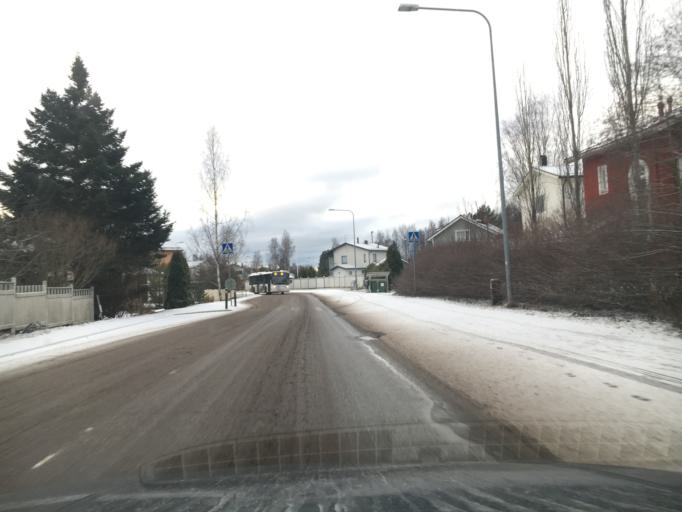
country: FI
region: Uusimaa
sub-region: Helsinki
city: Espoo
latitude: 60.1619
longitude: 24.6473
